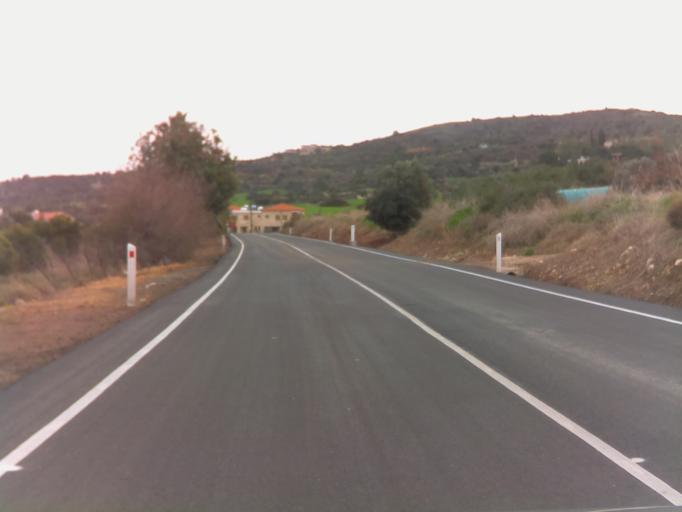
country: CY
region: Pafos
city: Polis
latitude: 35.0491
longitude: 32.3540
